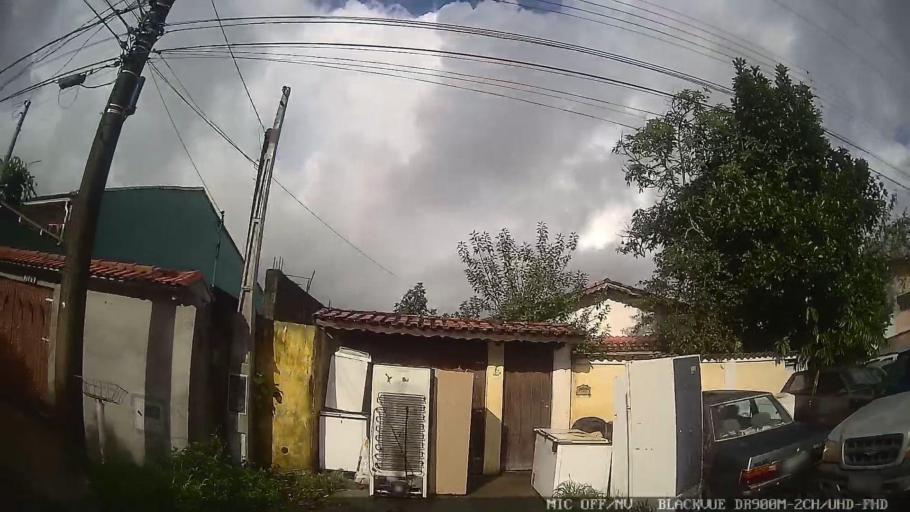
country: BR
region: Sao Paulo
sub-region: Itanhaem
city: Itanhaem
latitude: -24.2218
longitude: -46.8876
